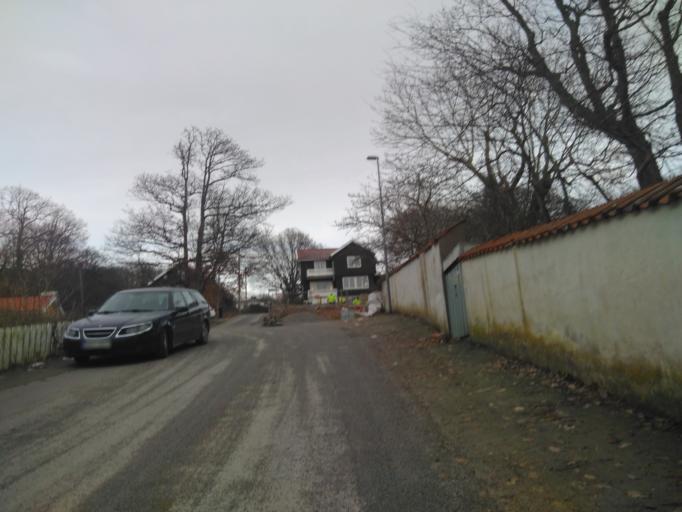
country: SE
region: Skane
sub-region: Hoganas Kommun
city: Hoganas
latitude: 56.2881
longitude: 12.4904
